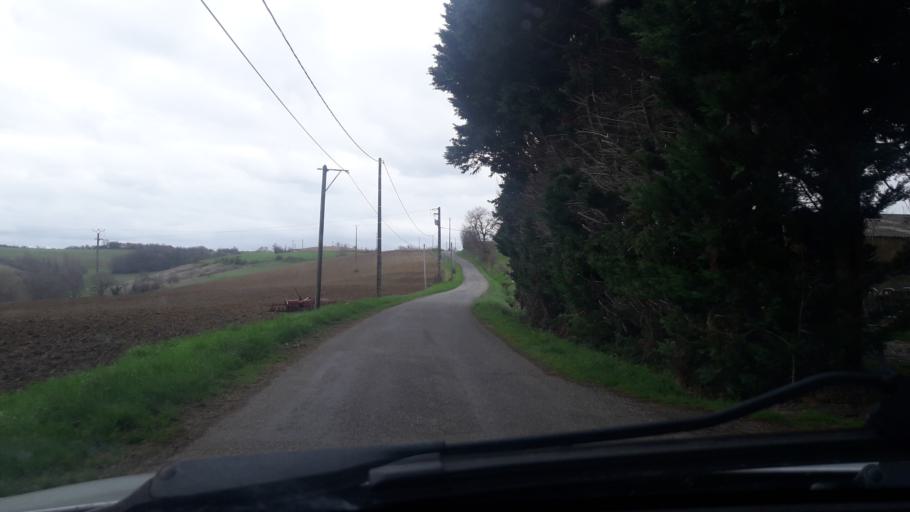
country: FR
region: Midi-Pyrenees
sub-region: Departement de l'Ariege
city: Lezat-sur-Leze
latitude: 43.2110
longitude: 1.3065
